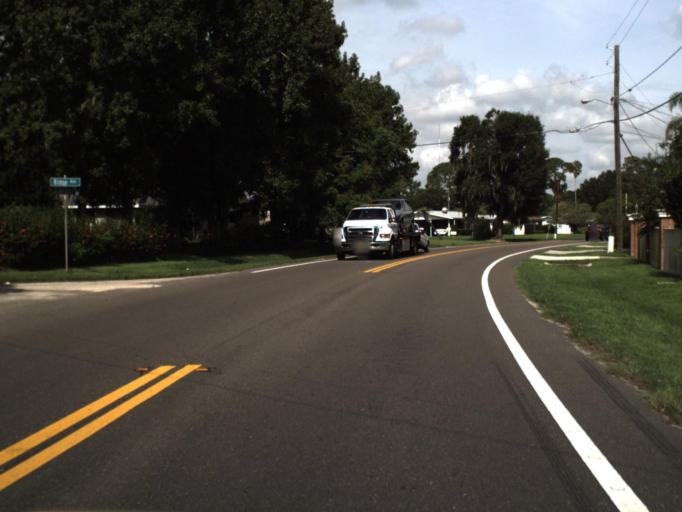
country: US
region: Florida
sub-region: Polk County
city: Eagle Lake
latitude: 27.9981
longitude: -81.7464
